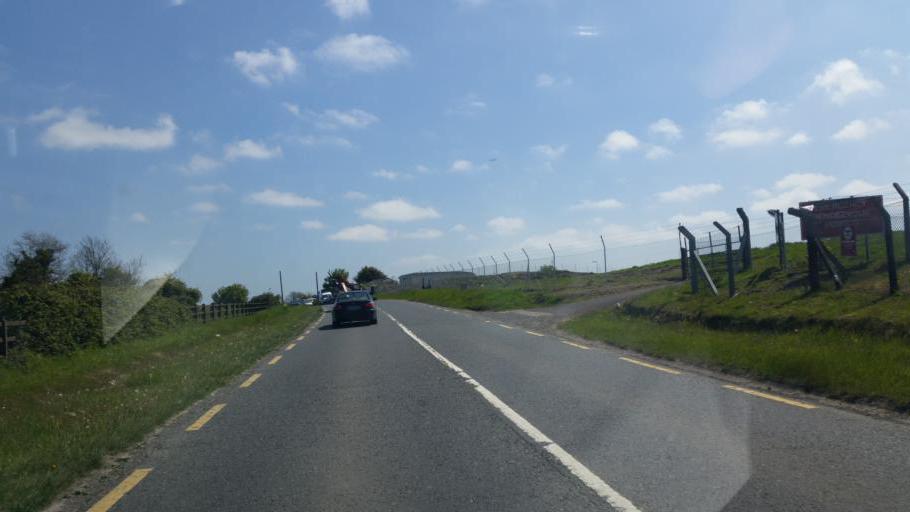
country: IE
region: Leinster
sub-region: Fingal County
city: Swords
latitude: 53.4367
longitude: -6.2375
